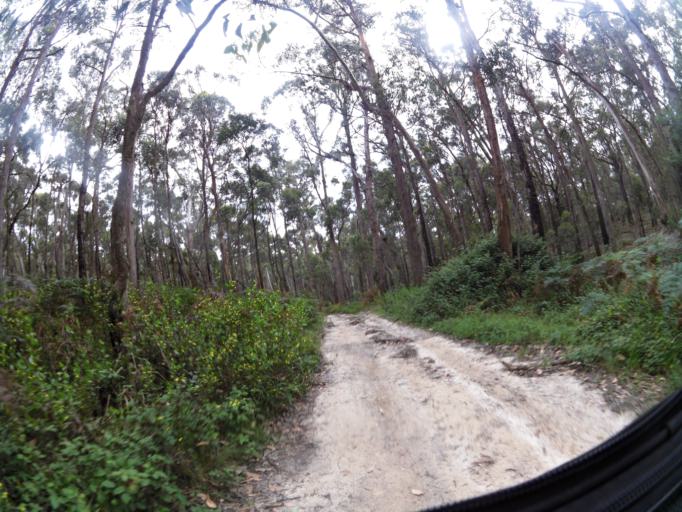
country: AU
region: Victoria
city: Brown Hill
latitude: -37.4998
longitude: 143.9077
